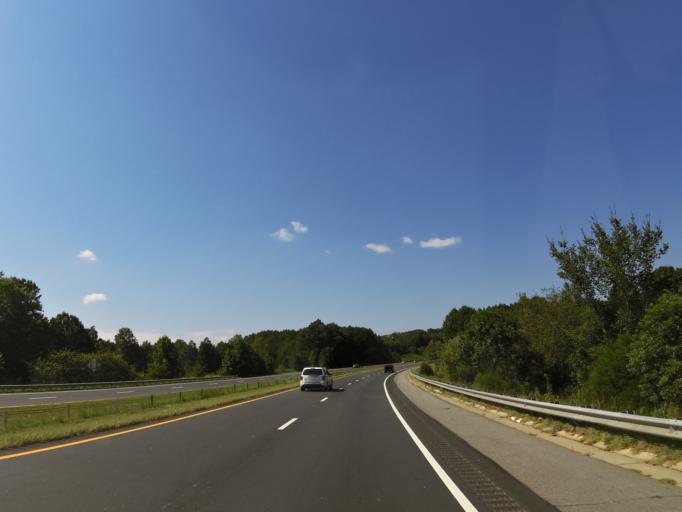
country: US
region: North Carolina
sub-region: Catawba County
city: Maiden
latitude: 35.5579
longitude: -81.2463
